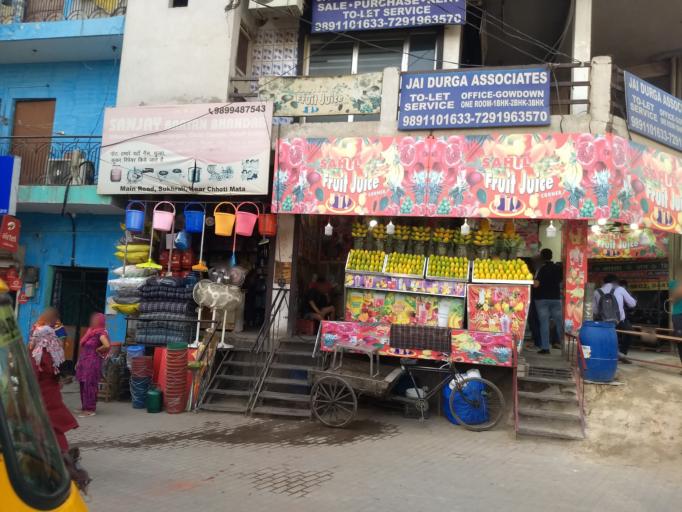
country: IN
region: Haryana
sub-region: Gurgaon
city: Gurgaon
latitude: 28.4760
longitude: 77.0619
